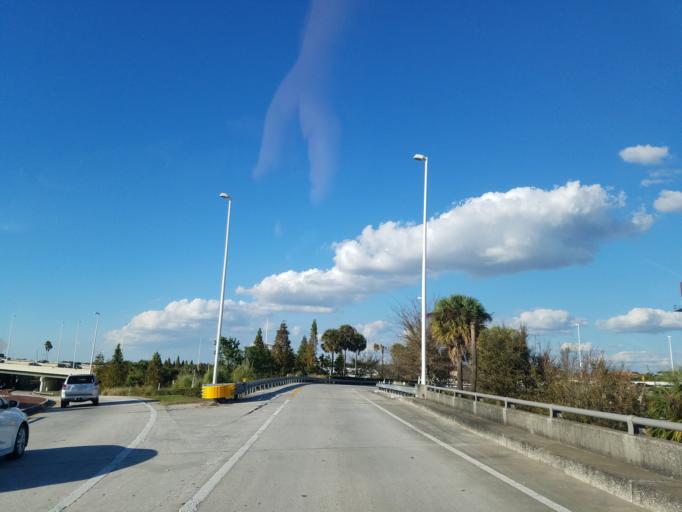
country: US
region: Florida
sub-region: Hillsborough County
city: Tampa
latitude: 27.9550
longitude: -82.4620
